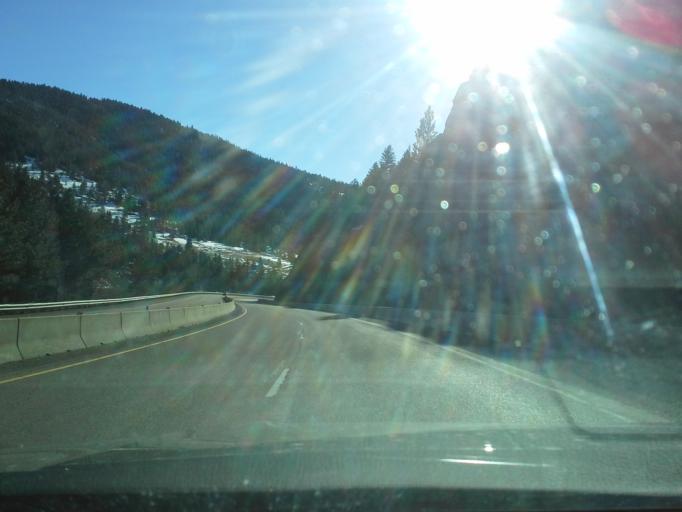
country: US
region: Montana
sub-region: Lewis and Clark County
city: Helena Valley Northwest
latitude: 46.9643
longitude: -112.0949
